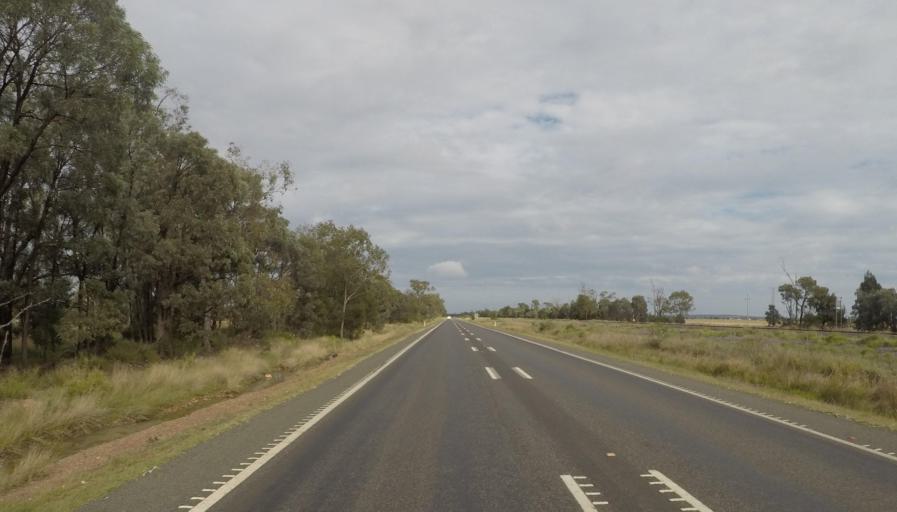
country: AU
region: Queensland
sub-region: Western Downs
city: Chinchilla
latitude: -26.6815
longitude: 150.4597
